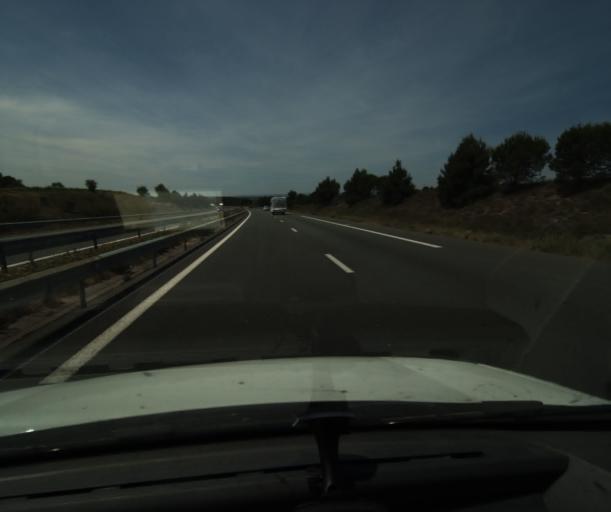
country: FR
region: Languedoc-Roussillon
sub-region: Departement de l'Aude
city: Capendu
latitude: 43.1765
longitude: 2.5966
